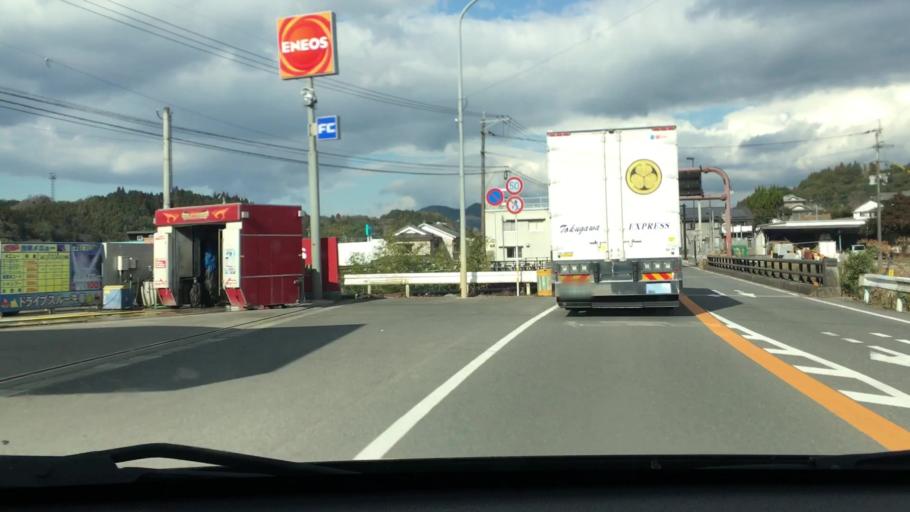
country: JP
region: Oita
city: Usuki
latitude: 33.0332
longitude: 131.6891
